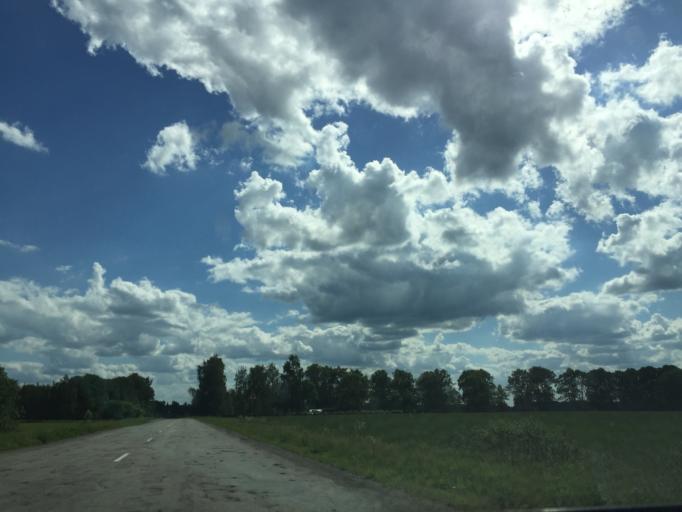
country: LV
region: Tukuma Rajons
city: Tukums
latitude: 56.8874
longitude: 23.0815
